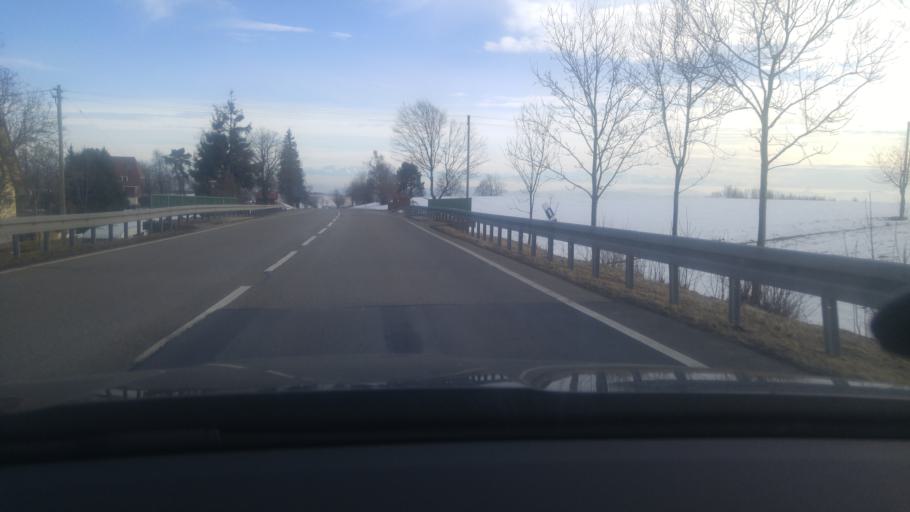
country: DE
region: Baden-Wuerttemberg
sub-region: Freiburg Region
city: Hochenschwand
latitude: 47.7032
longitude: 8.1441
